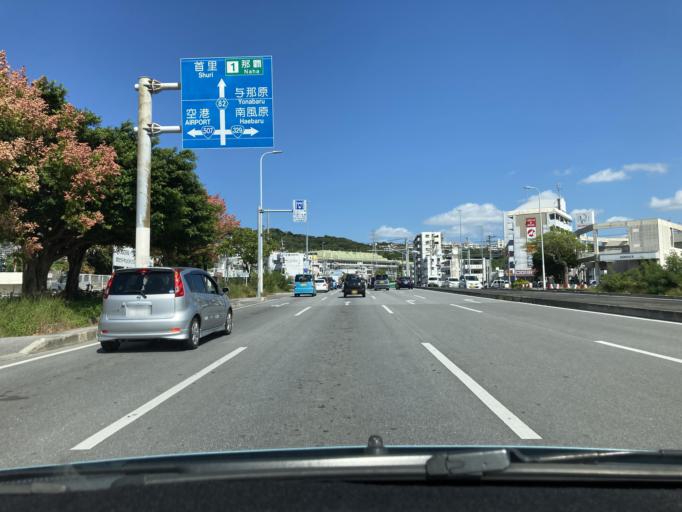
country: JP
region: Okinawa
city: Tomigusuku
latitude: 26.1974
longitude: 127.7132
